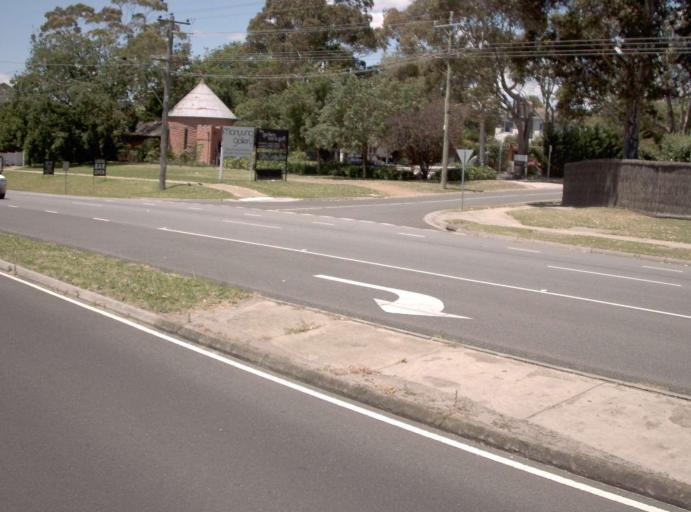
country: AU
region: Victoria
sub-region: Mornington Peninsula
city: Mount Eliza
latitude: -38.1992
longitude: 145.0840
